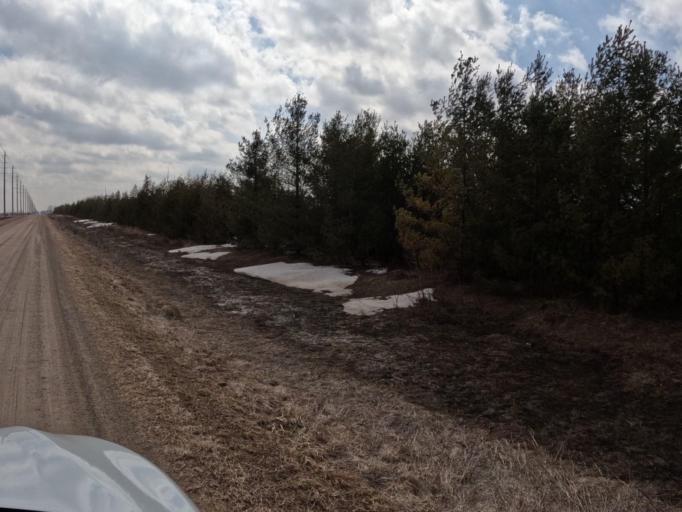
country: CA
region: Ontario
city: Shelburne
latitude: 44.0494
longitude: -80.3196
